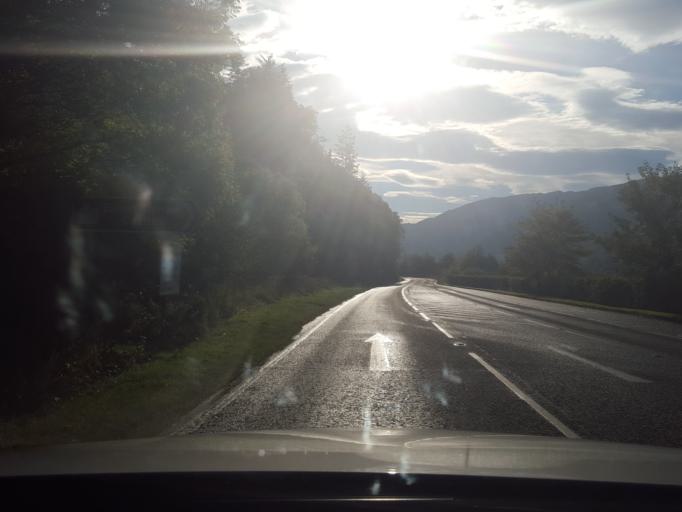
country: GB
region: Scotland
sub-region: Highland
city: Fort William
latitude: 57.2742
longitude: -5.5128
